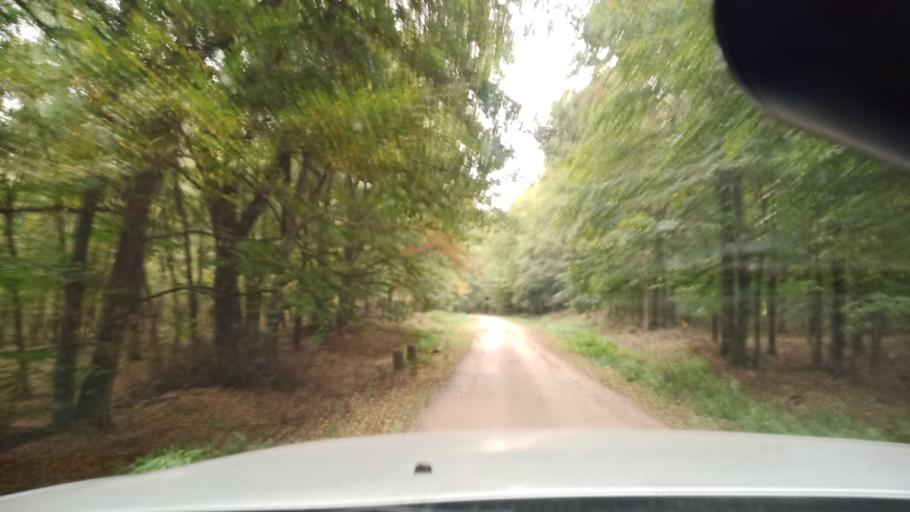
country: HU
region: Fejer
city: Pusztavam
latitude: 47.3879
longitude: 18.2858
